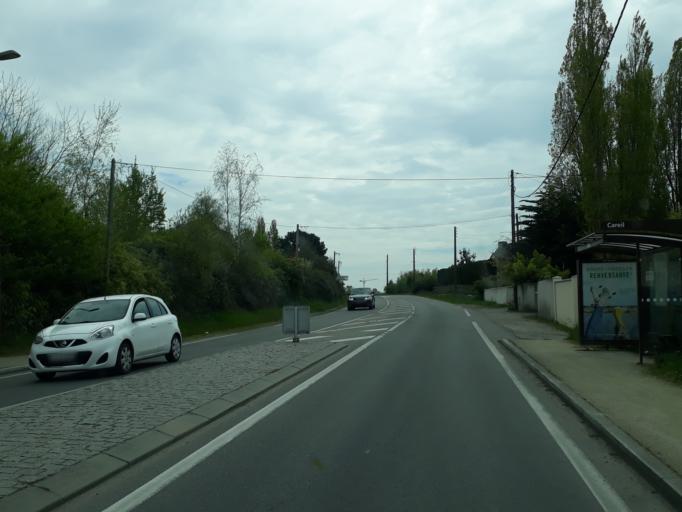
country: FR
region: Pays de la Loire
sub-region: Departement de la Loire-Atlantique
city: Le Pouliguen
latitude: 47.2978
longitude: -2.4058
